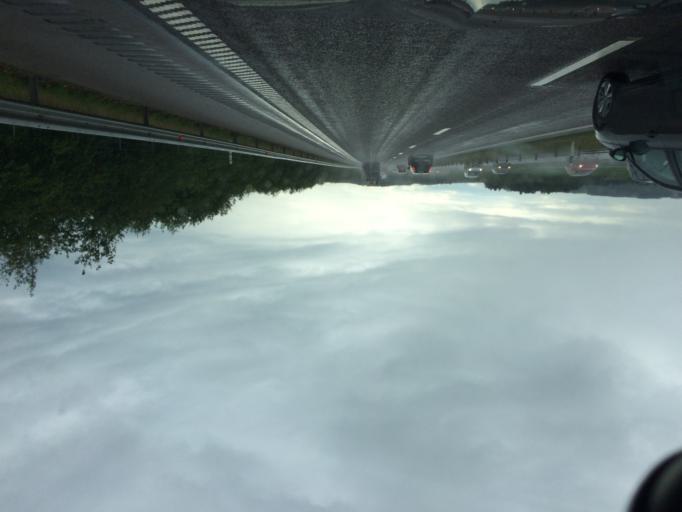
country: SE
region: Halland
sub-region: Halmstads Kommun
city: Getinge
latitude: 56.8019
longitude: 12.7650
